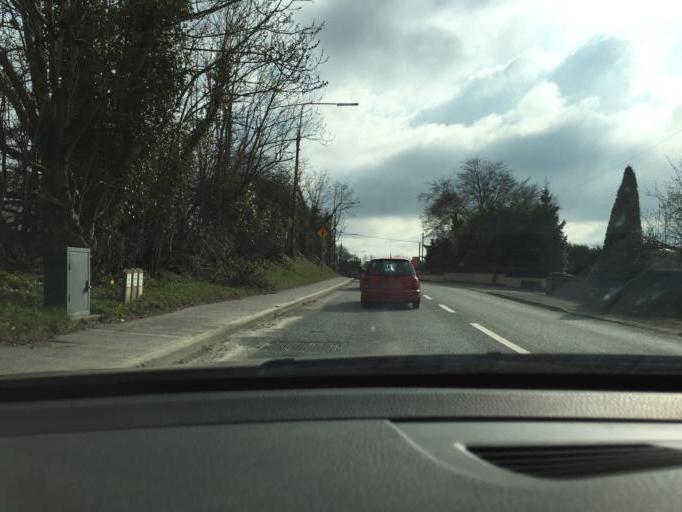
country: IE
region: Leinster
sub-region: Wicklow
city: Blessington
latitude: 53.1772
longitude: -6.5262
